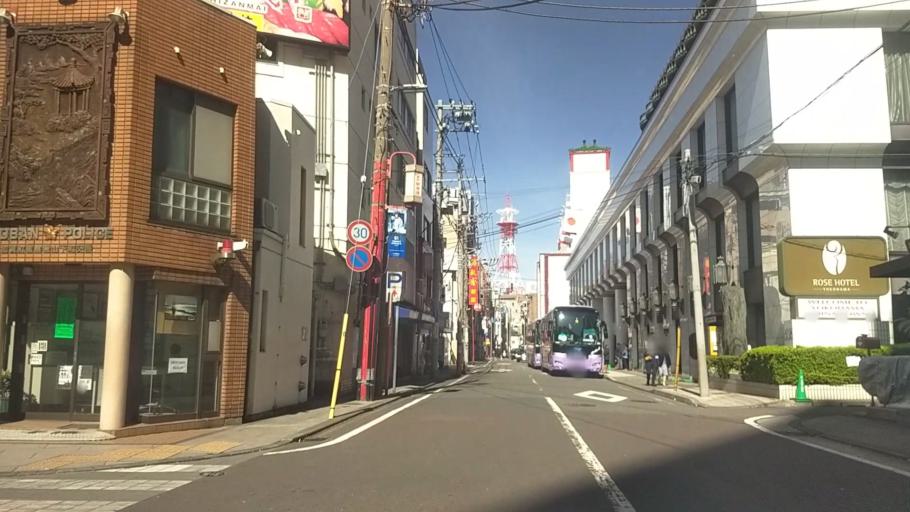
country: JP
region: Kanagawa
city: Yokohama
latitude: 35.4437
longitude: 139.6475
